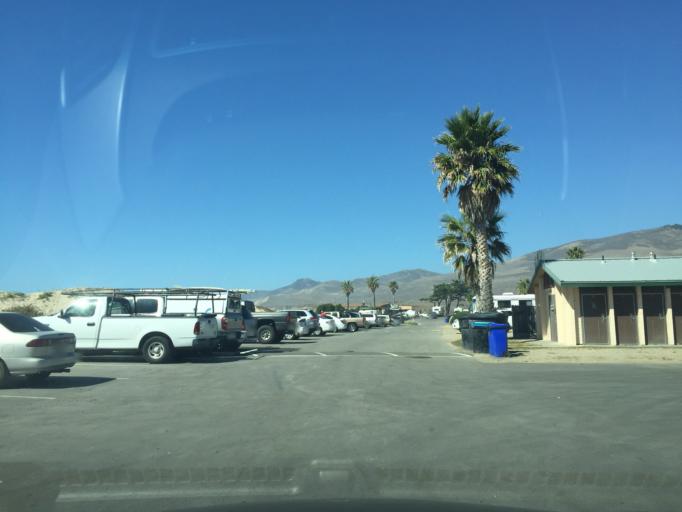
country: US
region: California
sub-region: Santa Barbara County
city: Lompoc
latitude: 34.5100
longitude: -120.5011
